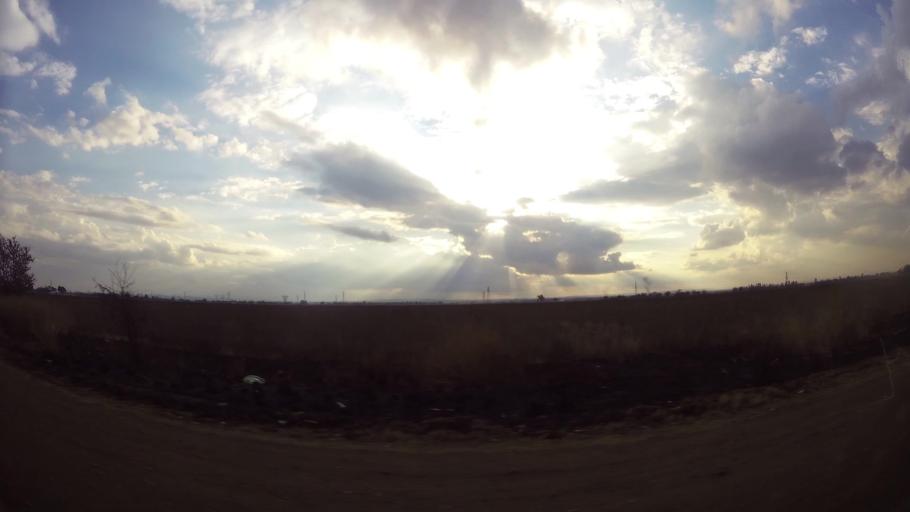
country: ZA
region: Gauteng
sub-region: Sedibeng District Municipality
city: Vanderbijlpark
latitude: -26.6702
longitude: 27.7936
